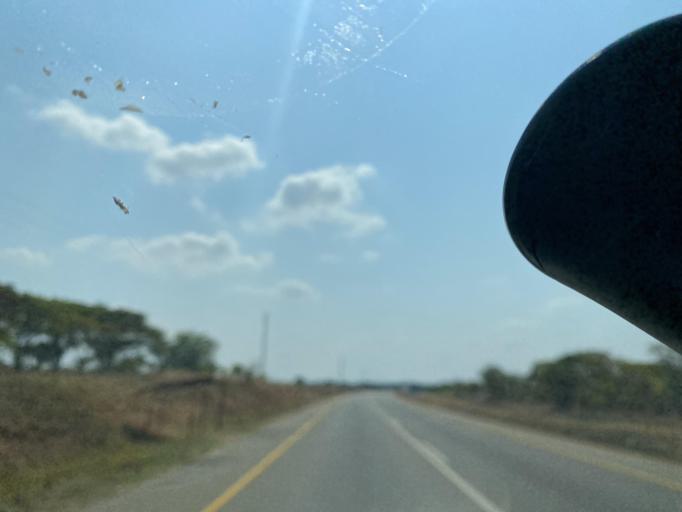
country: ZM
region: Lusaka
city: Chongwe
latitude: -15.5294
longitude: 28.6176
